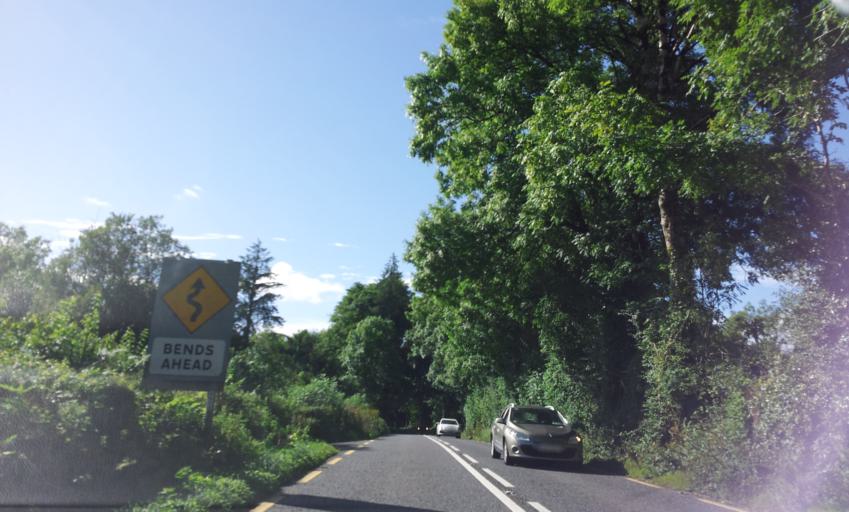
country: IE
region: Munster
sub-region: County Cork
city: Millstreet
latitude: 51.9249
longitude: -9.1004
